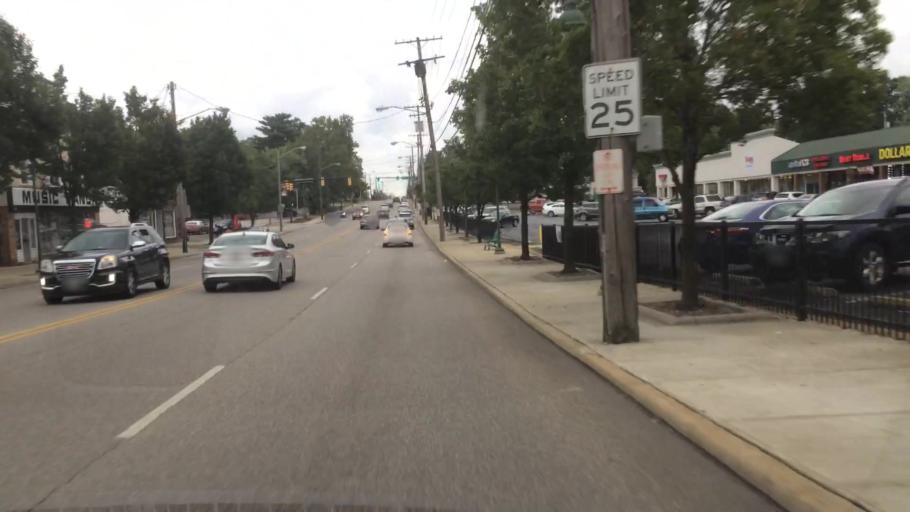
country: US
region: Ohio
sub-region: Cuyahoga County
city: Maple Heights
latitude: 41.4166
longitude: -81.5717
